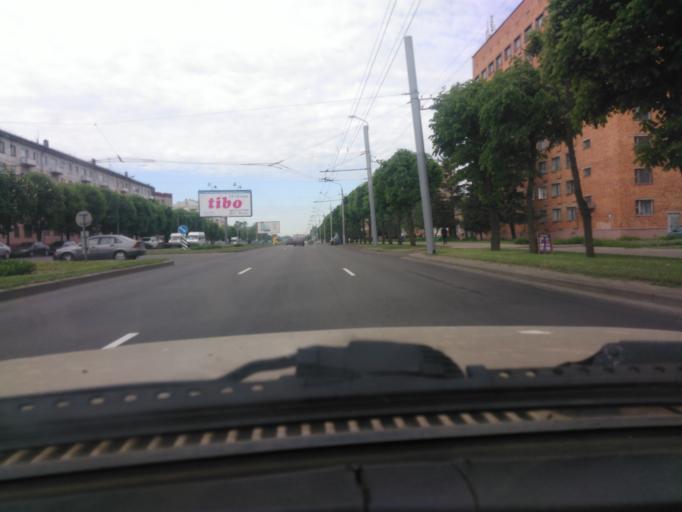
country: BY
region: Mogilev
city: Mahilyow
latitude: 53.9108
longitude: 30.3149
